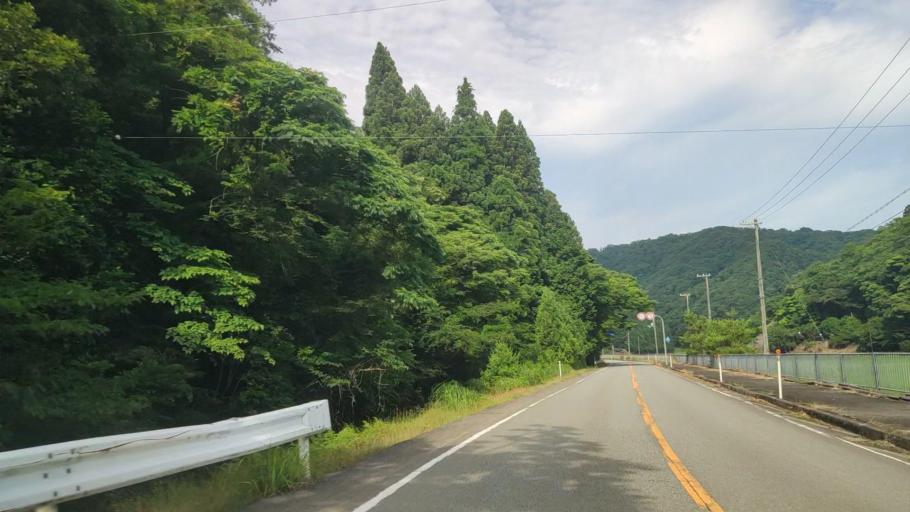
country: JP
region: Hyogo
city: Toyooka
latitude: 35.6156
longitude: 134.8489
